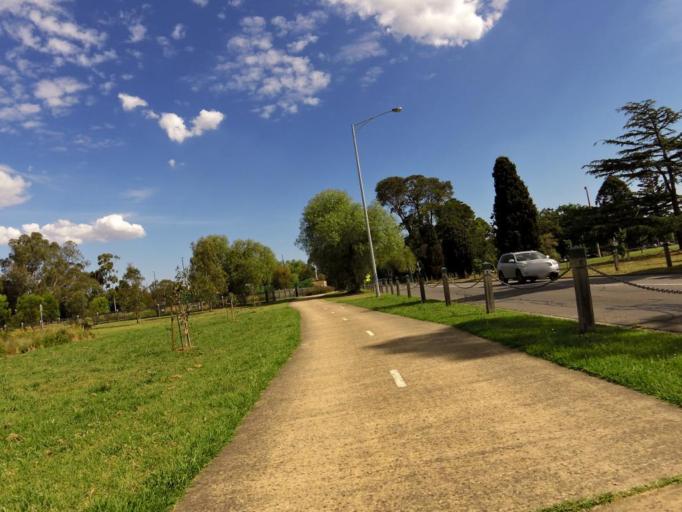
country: AU
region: Victoria
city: Rosanna
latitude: -37.7537
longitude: 145.0745
